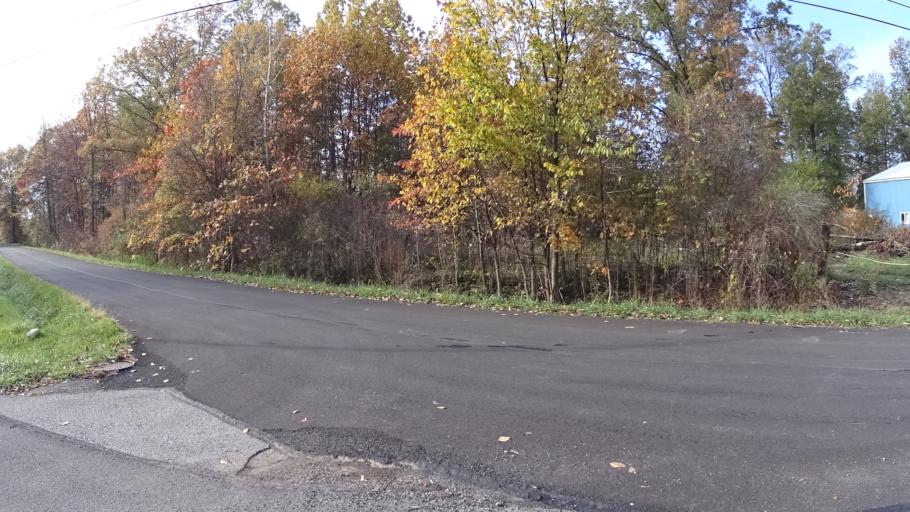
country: US
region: Ohio
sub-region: Lorain County
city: Lorain
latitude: 41.4332
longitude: -82.1410
